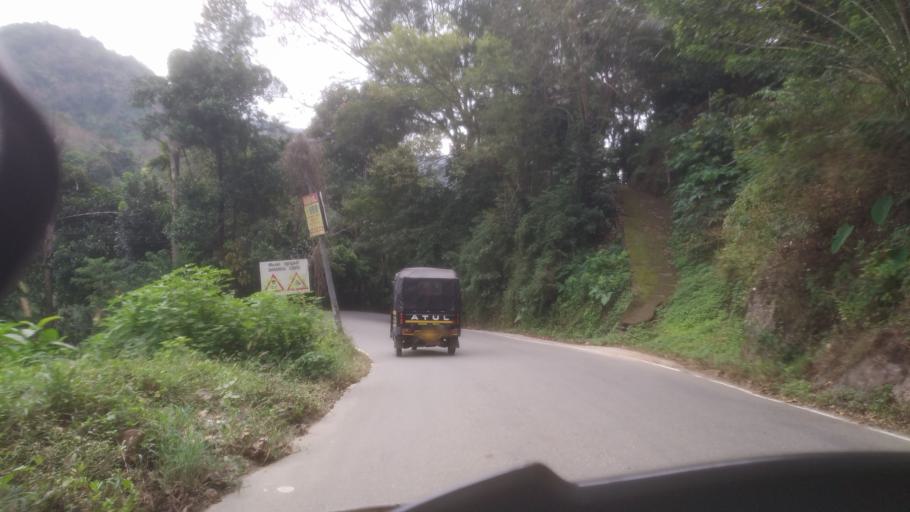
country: IN
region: Kerala
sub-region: Idukki
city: Munnar
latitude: 9.9795
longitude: 77.0001
